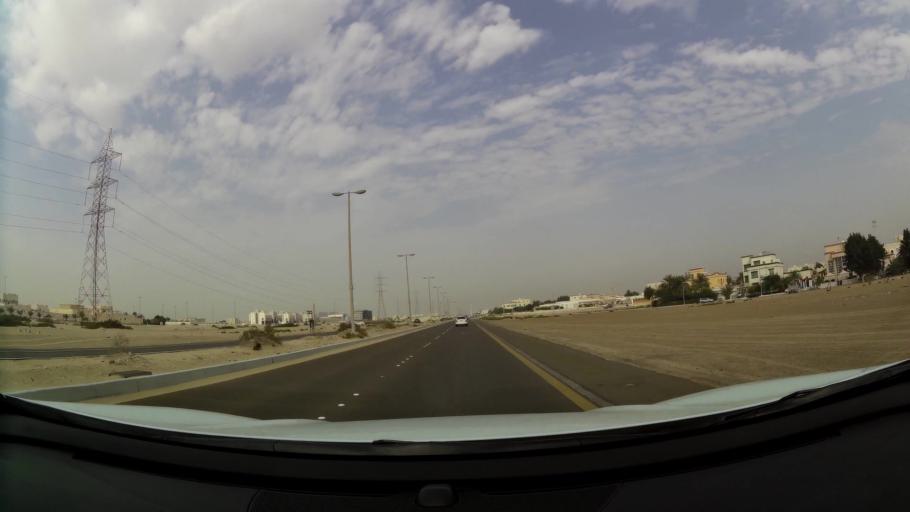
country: AE
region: Abu Dhabi
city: Abu Dhabi
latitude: 24.3156
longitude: 54.6373
